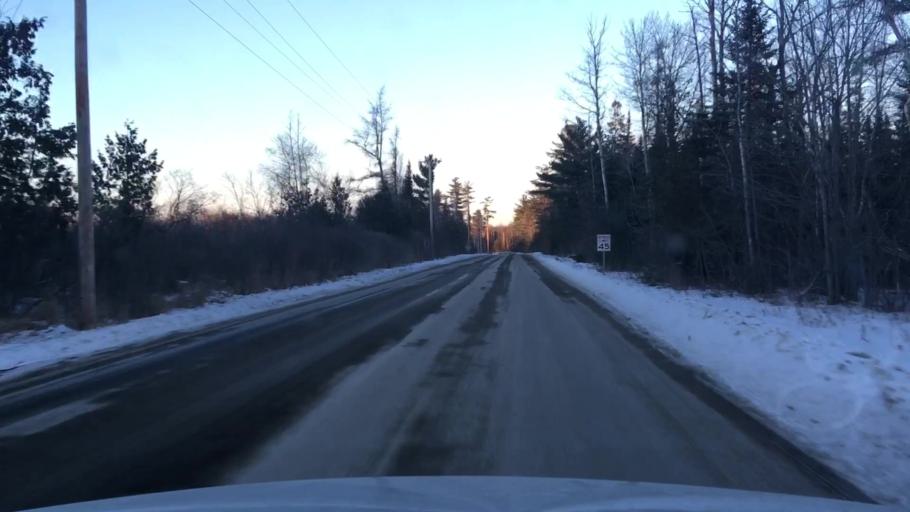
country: US
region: Maine
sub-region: Penobscot County
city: Orrington
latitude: 44.7086
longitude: -68.7545
